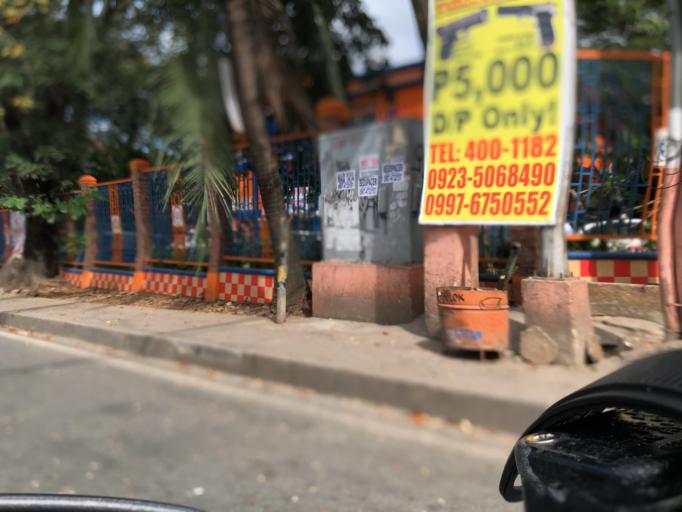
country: PH
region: Central Luzon
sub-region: Province of Bulacan
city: San Jose del Monte
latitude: 14.7495
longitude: 121.0533
